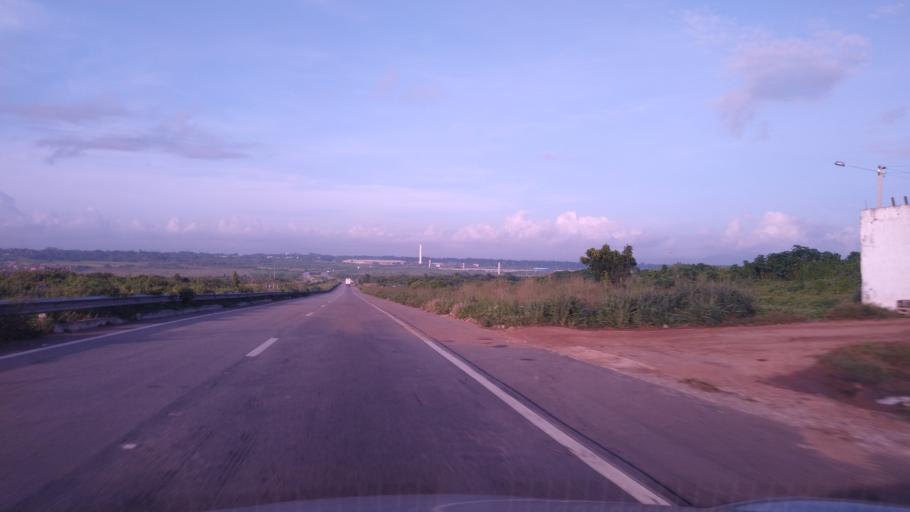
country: BR
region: Ceara
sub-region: Pacajus
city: Pacajus
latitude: -4.1504
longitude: -38.4790
